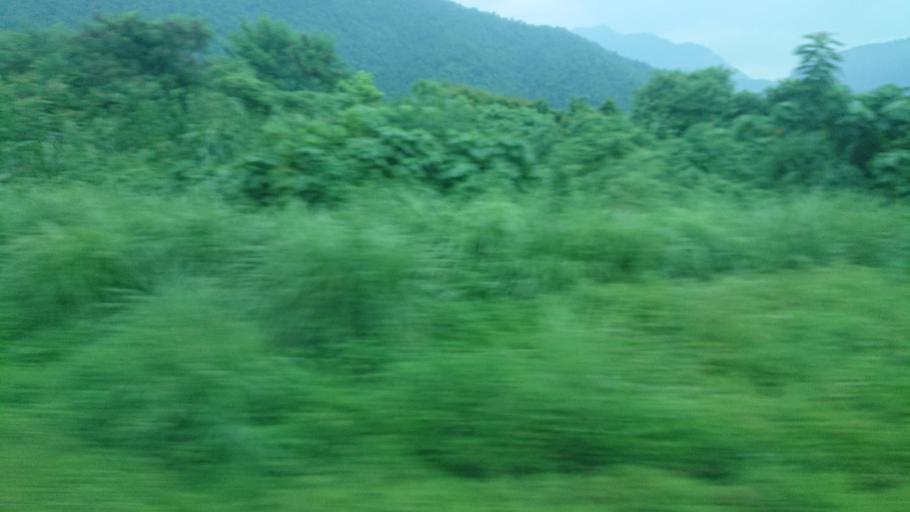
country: TW
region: Taiwan
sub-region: Hualien
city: Hualian
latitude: 24.1213
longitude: 121.6357
